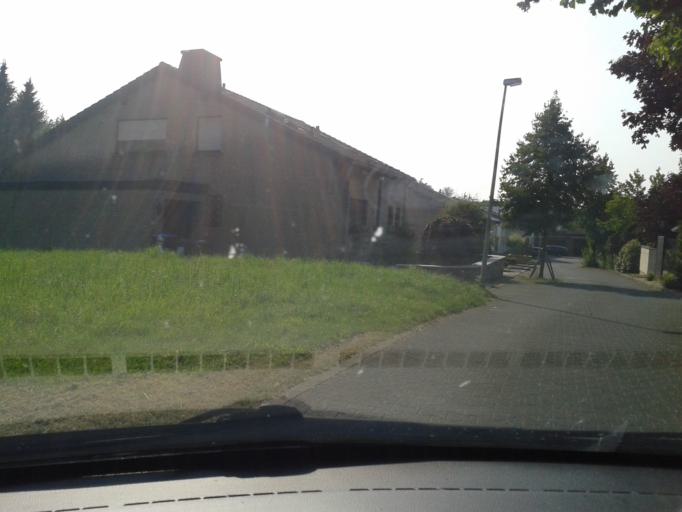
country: DE
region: North Rhine-Westphalia
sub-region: Regierungsbezirk Detmold
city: Paderborn
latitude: 51.7044
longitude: 8.7840
